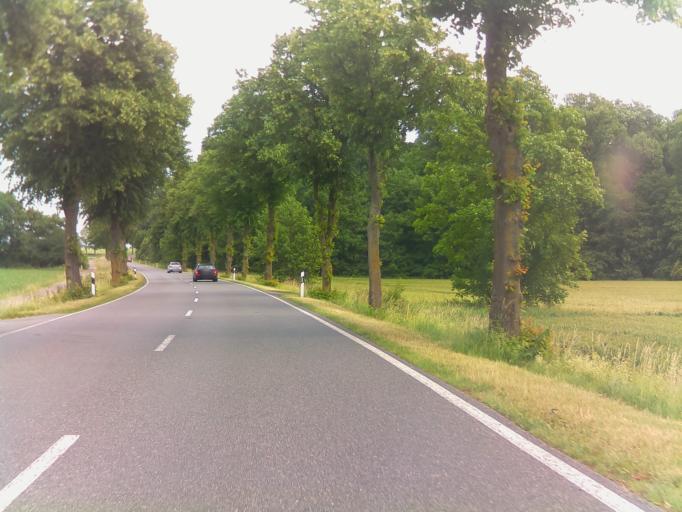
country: DE
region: Lower Saxony
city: Springe
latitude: 52.1756
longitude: 9.6096
